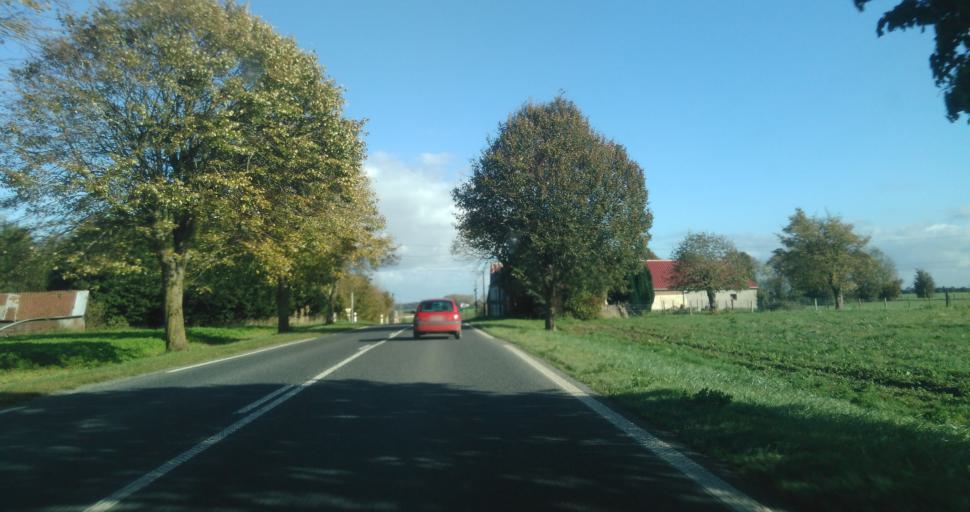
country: FR
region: Nord-Pas-de-Calais
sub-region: Departement du Pas-de-Calais
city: Beaumetz-les-Loges
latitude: 50.2211
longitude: 2.5901
